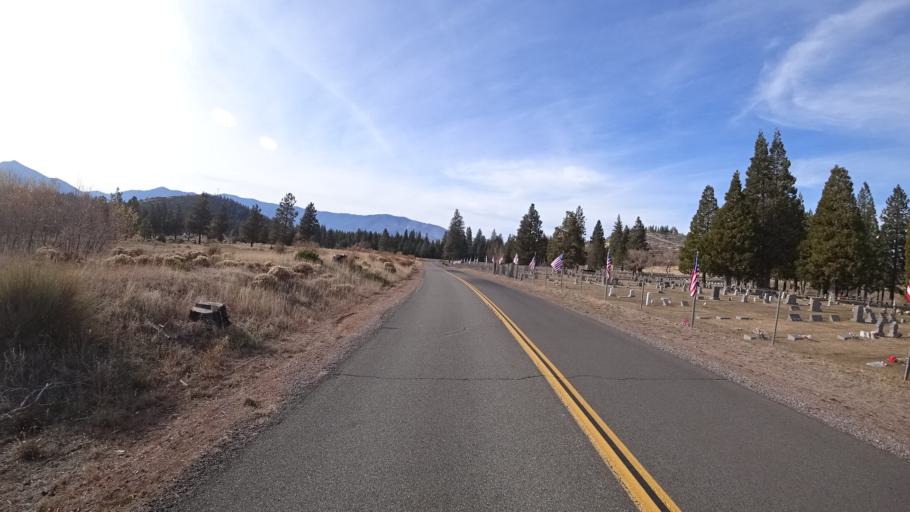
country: US
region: California
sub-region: Siskiyou County
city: Weed
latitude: 41.4396
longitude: -122.3829
